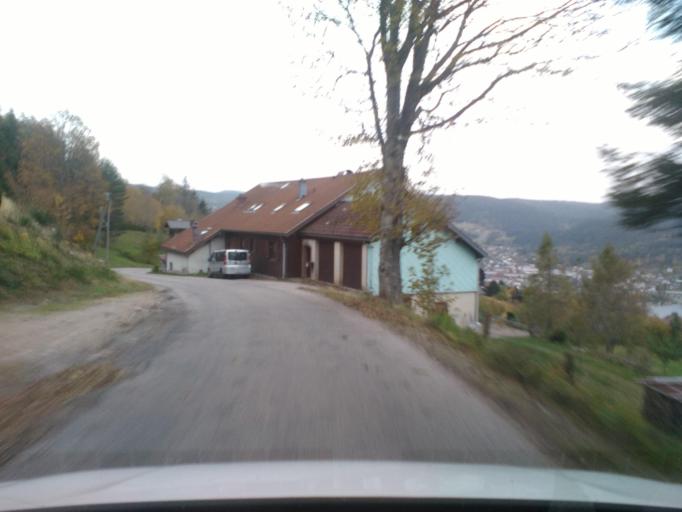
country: FR
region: Lorraine
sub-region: Departement des Vosges
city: Gerardmer
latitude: 48.0831
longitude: 6.8605
